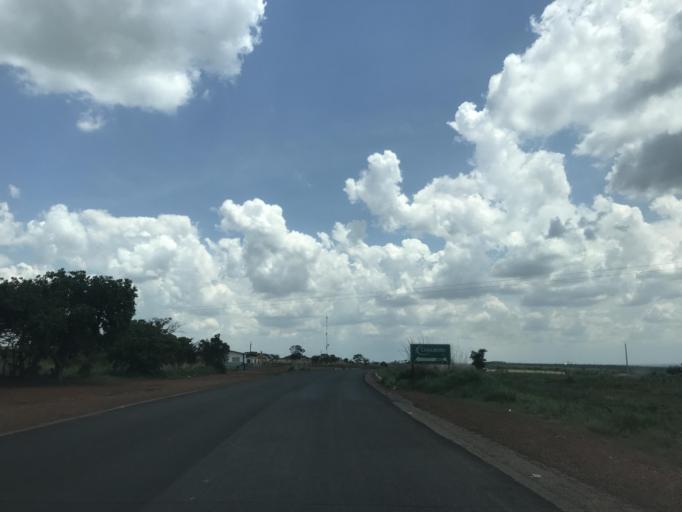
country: BR
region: Goias
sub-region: Piracanjuba
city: Piracanjuba
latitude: -17.3420
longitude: -48.7928
